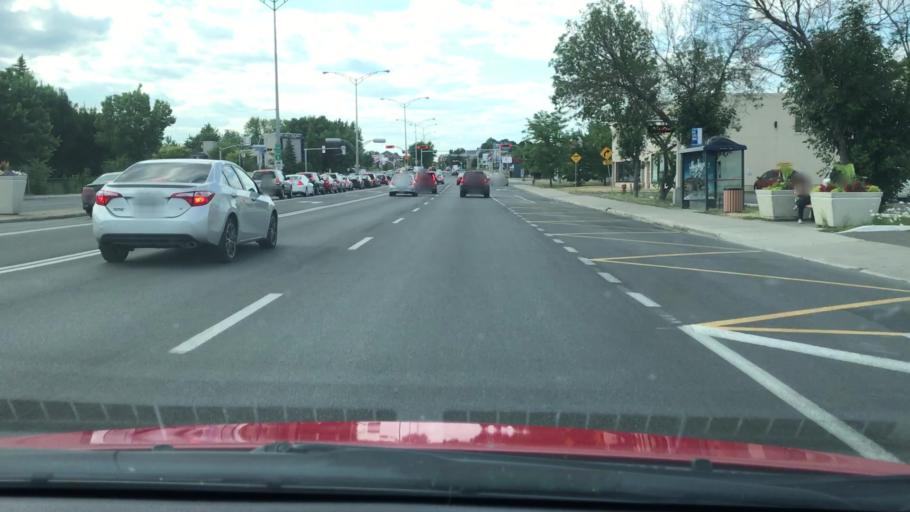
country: CA
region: Quebec
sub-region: Laval
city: Laval
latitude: 45.5358
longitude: -73.7308
